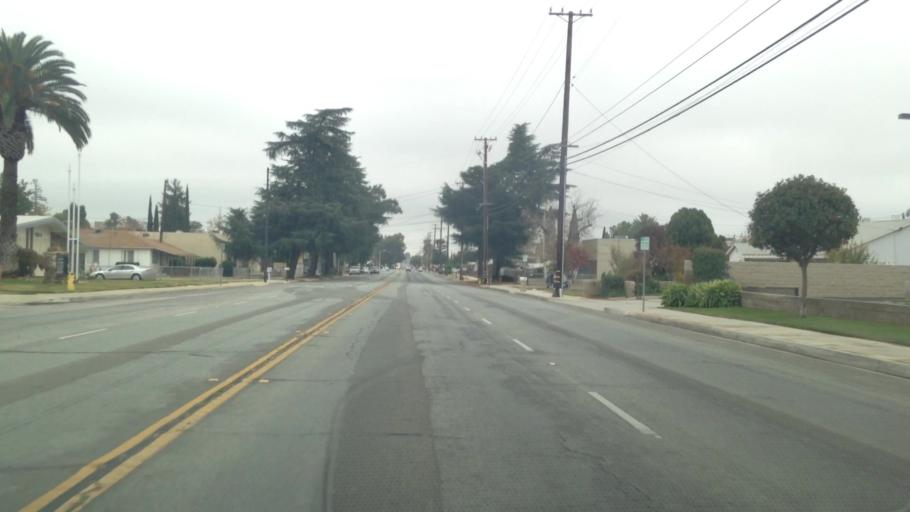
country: US
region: California
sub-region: Riverside County
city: Beaumont
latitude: 33.9396
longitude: -116.9773
